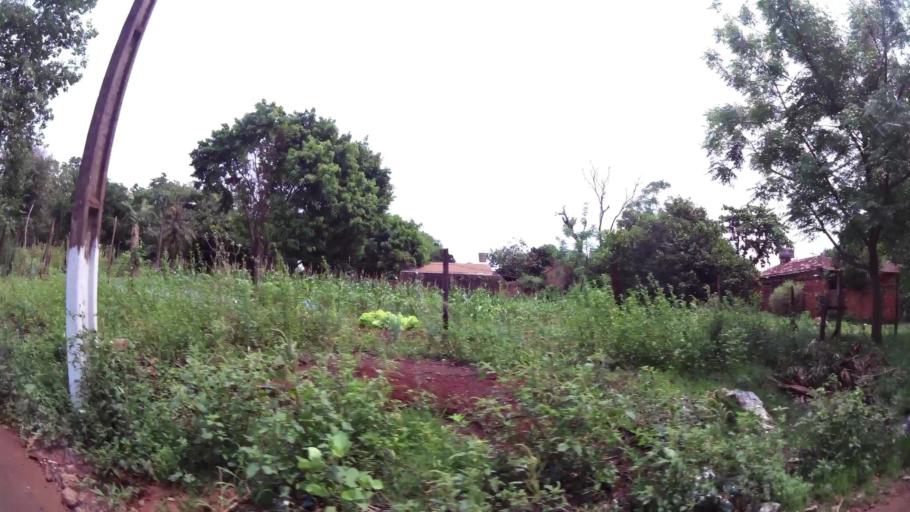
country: BR
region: Parana
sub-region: Foz Do Iguacu
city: Foz do Iguacu
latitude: -25.5727
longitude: -54.6049
